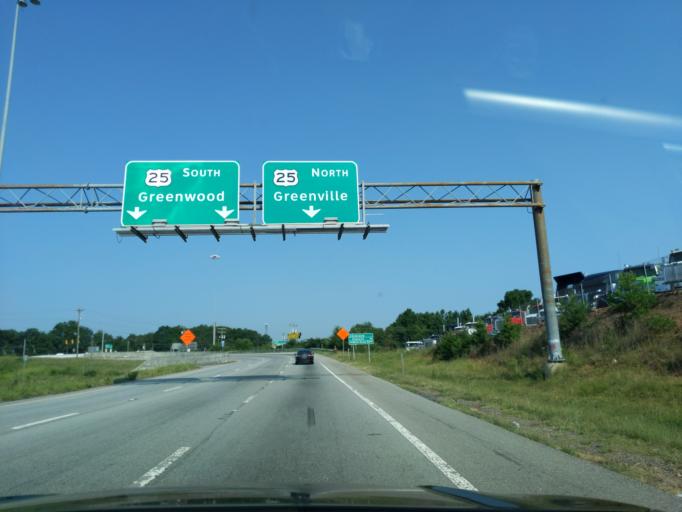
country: US
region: South Carolina
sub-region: Greenville County
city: Gantt
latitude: 34.7923
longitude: -82.4152
